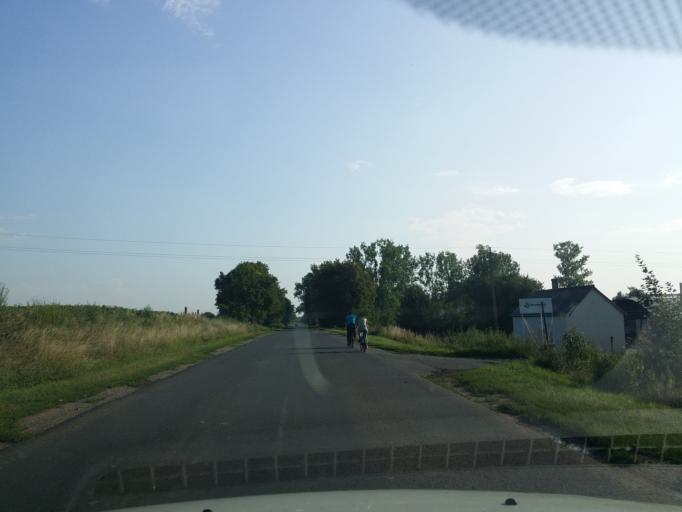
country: HU
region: Borsod-Abauj-Zemplen
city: Gonc
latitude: 48.3955
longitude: 21.2238
